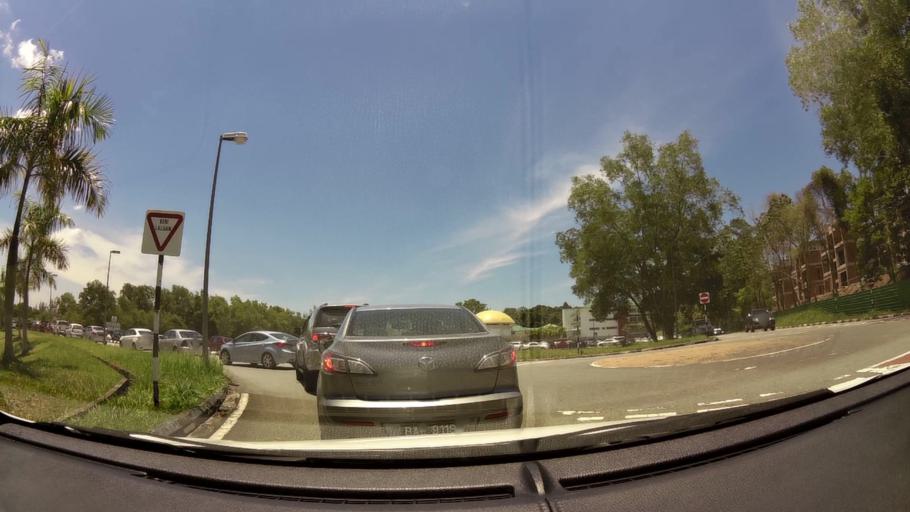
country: BN
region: Brunei and Muara
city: Bandar Seri Begawan
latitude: 4.9245
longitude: 114.9629
